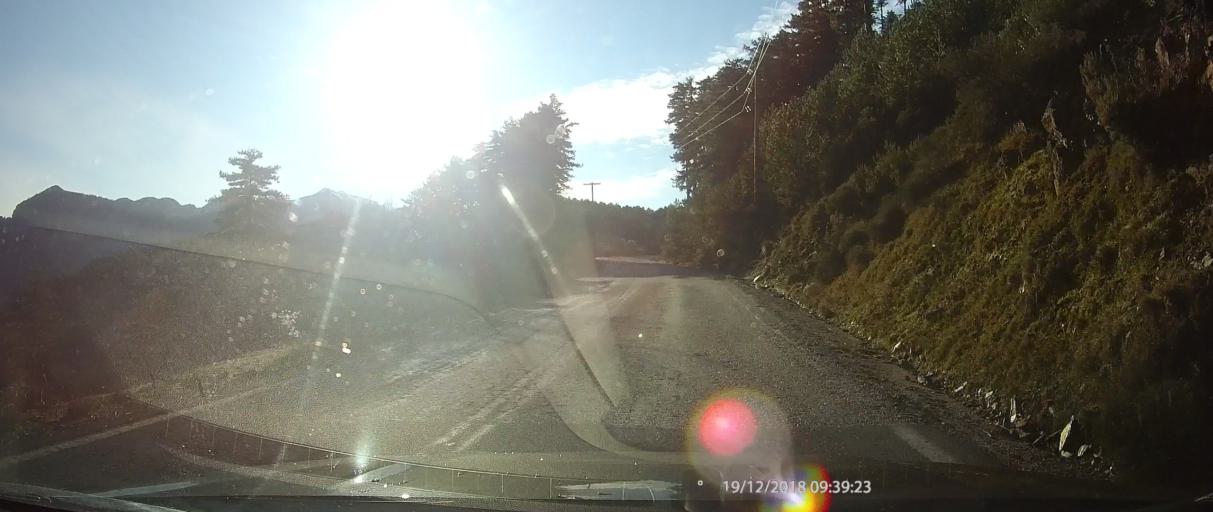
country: GR
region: Peloponnese
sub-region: Nomos Lakonias
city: Magoula
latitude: 37.0790
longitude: 22.2715
